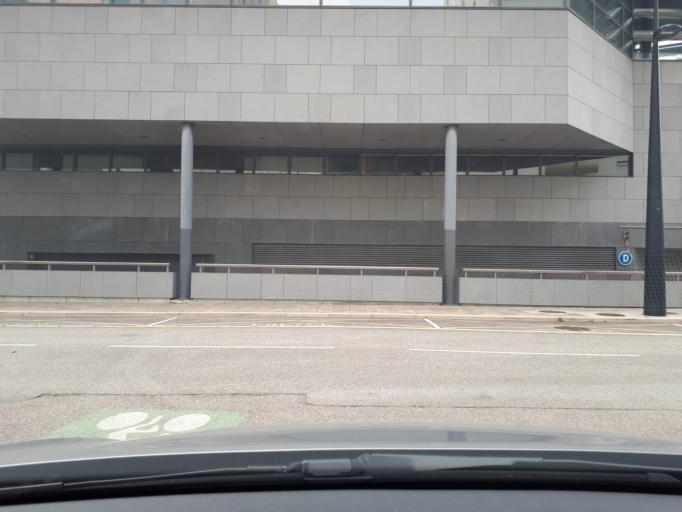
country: FR
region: Rhone-Alpes
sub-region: Departement de l'Isere
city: Saint-Martin-le-Vinoux
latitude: 45.1930
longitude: 5.7114
